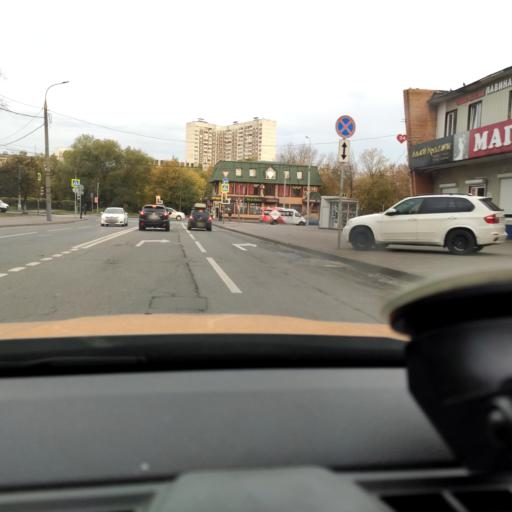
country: RU
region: Moscow
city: Lyublino
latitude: 55.6839
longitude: 37.7515
